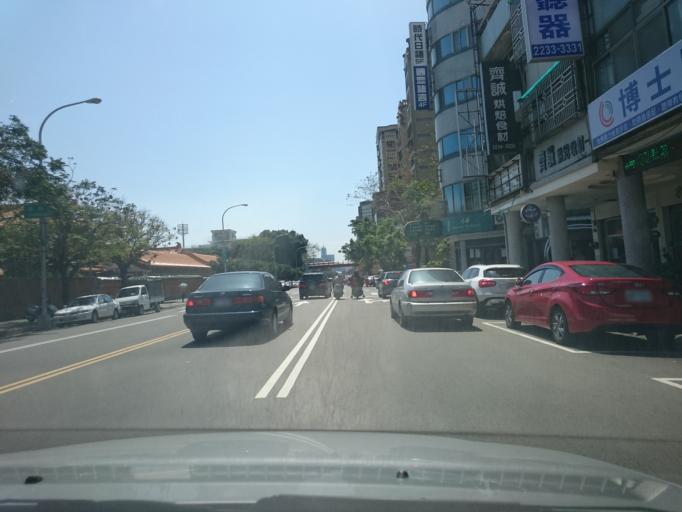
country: TW
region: Taiwan
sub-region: Taichung City
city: Taichung
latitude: 24.1553
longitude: 120.6898
